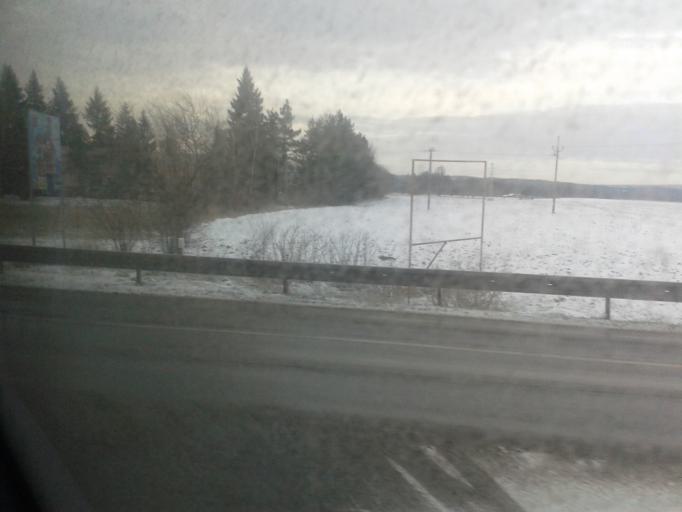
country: CZ
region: Olomoucky
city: Smrzice
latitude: 49.4868
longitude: 17.0947
